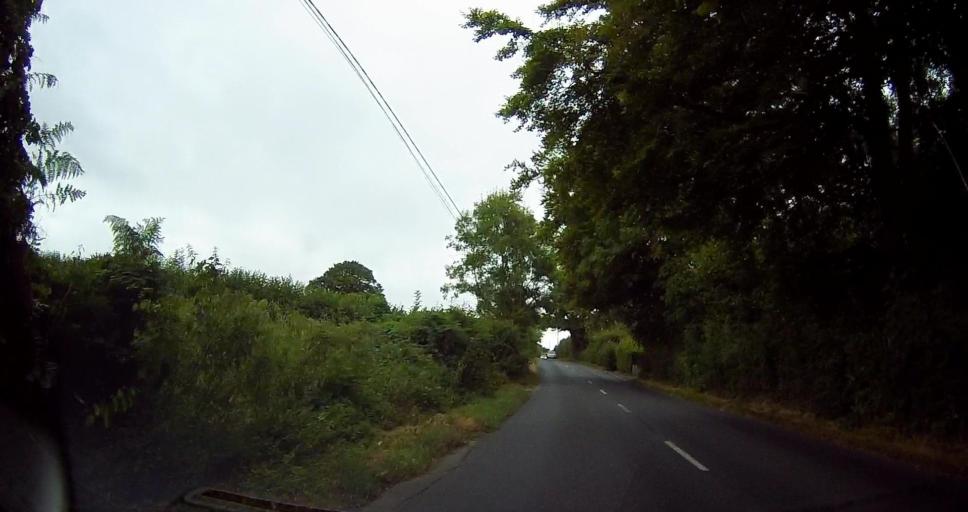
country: GB
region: England
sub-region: East Sussex
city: Wadhurst
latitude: 51.0867
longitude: 0.3827
